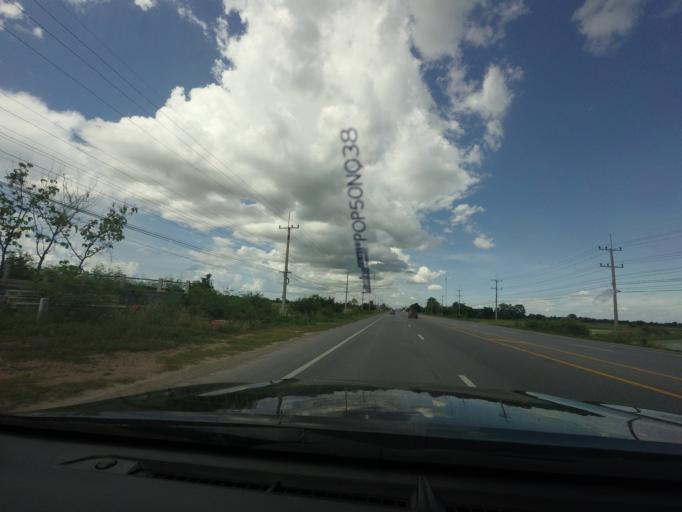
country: TH
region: Kanchanaburi
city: Phanom Thuan
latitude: 14.1589
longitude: 99.7149
